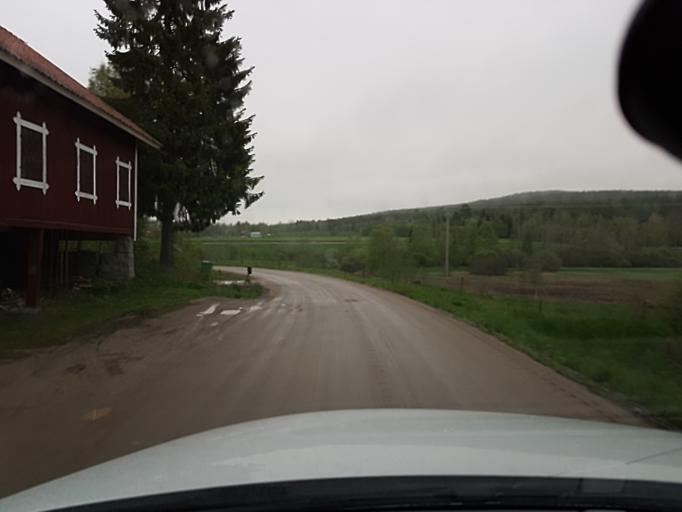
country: SE
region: Gaevleborg
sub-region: Ljusdals Kommun
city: Jaervsoe
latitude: 61.7536
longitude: 16.1922
